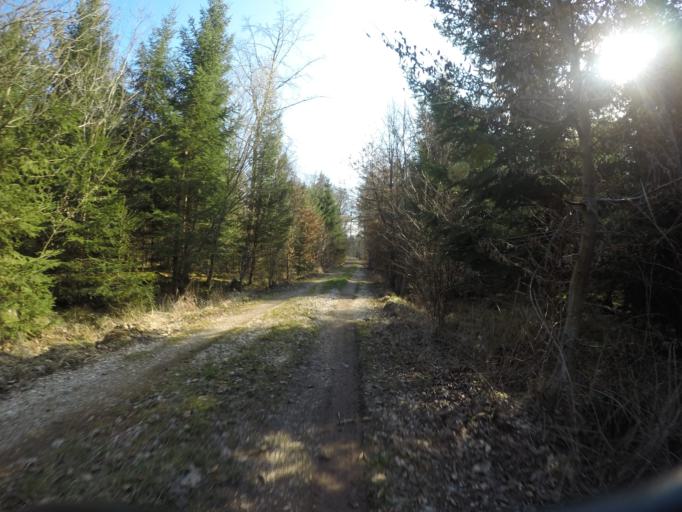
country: DE
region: Baden-Wuerttemberg
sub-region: Tuebingen Region
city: Dusslingen
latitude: 48.4642
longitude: 9.0267
